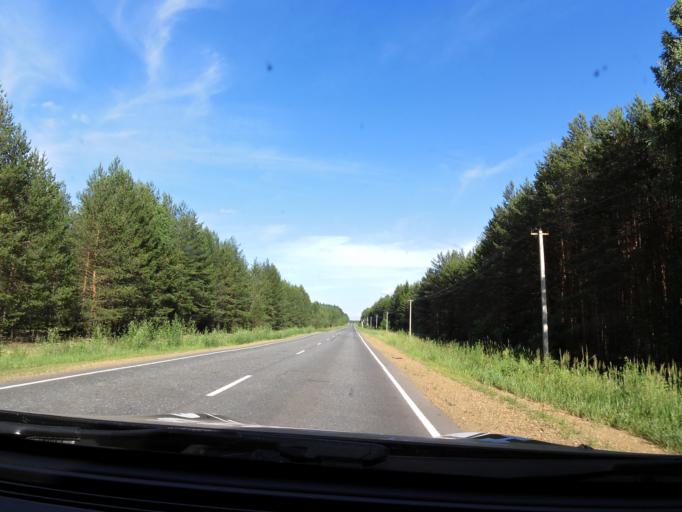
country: RU
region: Kirov
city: Belaya Kholunitsa
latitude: 58.9070
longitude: 51.0106
